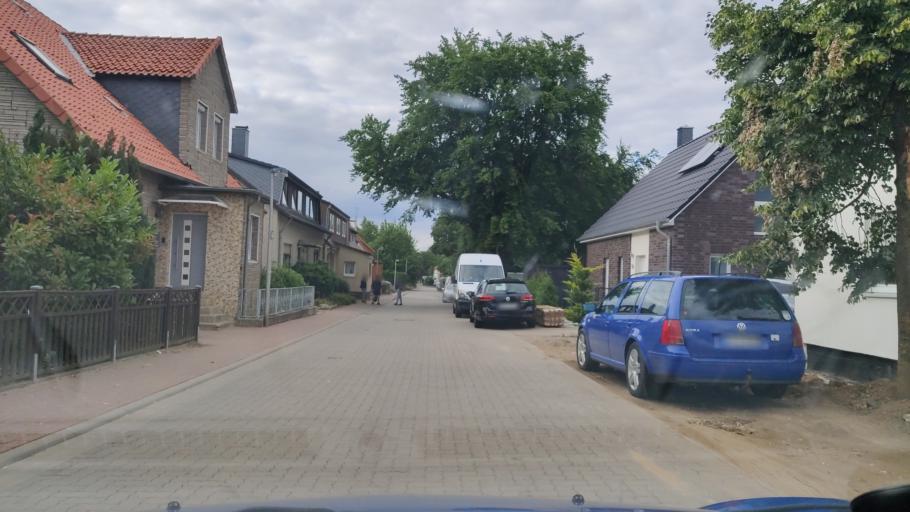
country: DE
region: Lower Saxony
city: Ronnenberg
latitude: 52.3137
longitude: 9.6562
